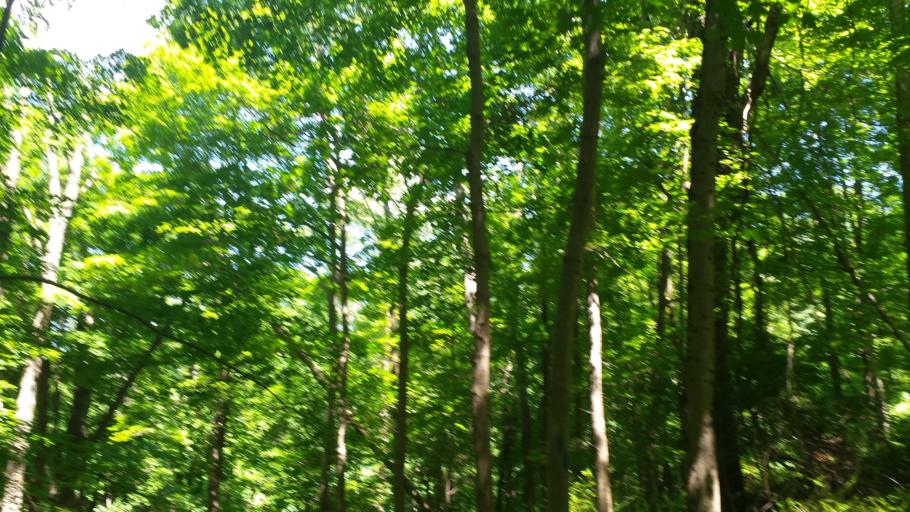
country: US
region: New York
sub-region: Westchester County
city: Mount Kisco
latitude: 41.1766
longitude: -73.7092
